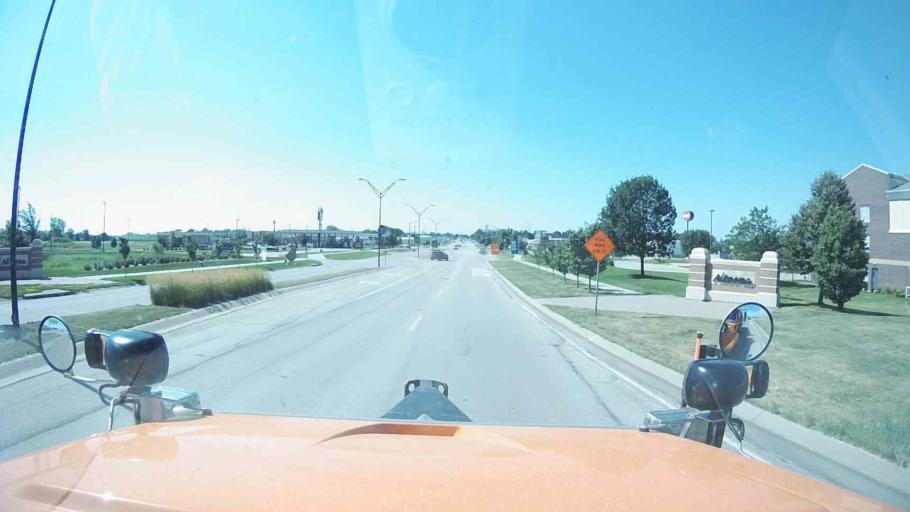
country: US
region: Iowa
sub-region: Polk County
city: Altoona
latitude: 41.6654
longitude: -93.4647
